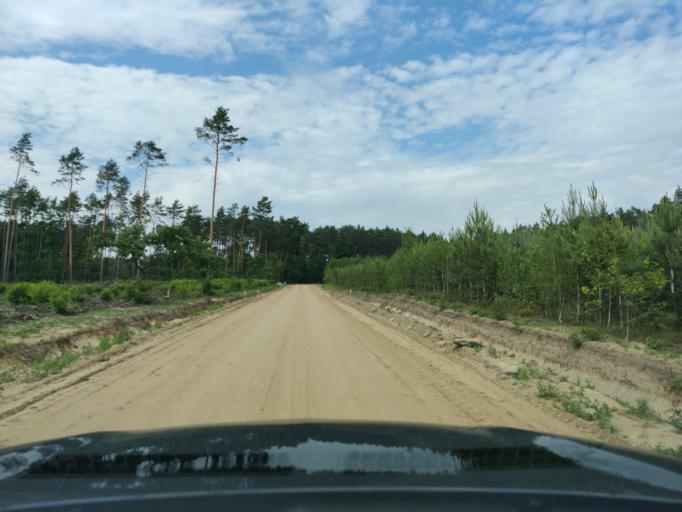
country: PL
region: Masovian Voivodeship
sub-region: Powiat pultuski
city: Pultusk
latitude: 52.7193
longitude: 21.1499
